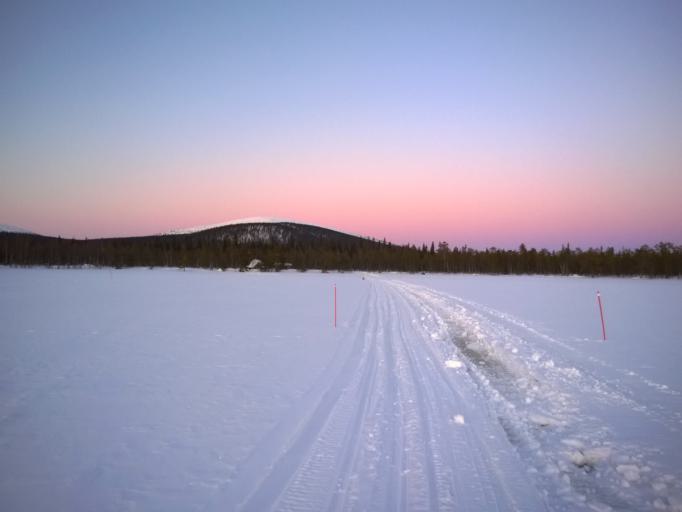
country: FI
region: Lapland
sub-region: Tunturi-Lappi
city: Muonio
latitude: 67.9330
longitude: 24.0509
